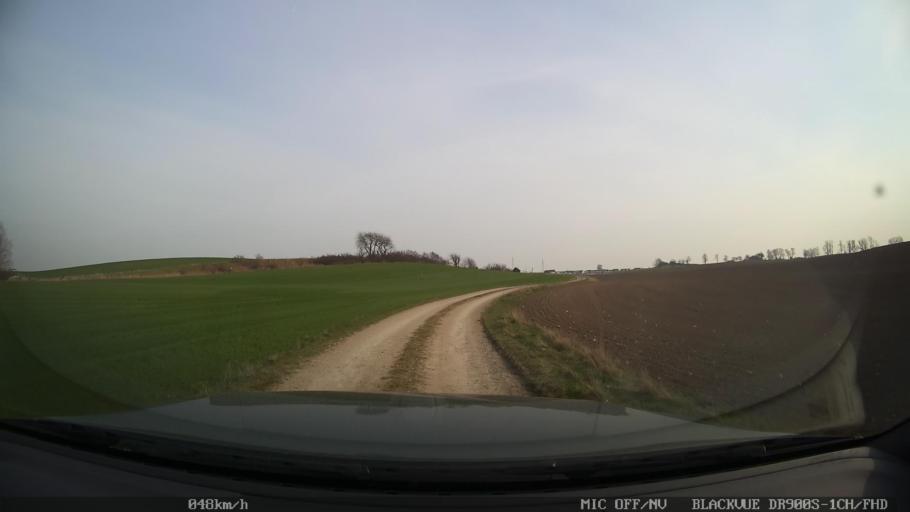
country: SE
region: Skane
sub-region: Ystads Kommun
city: Ystad
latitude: 55.4547
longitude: 13.7924
